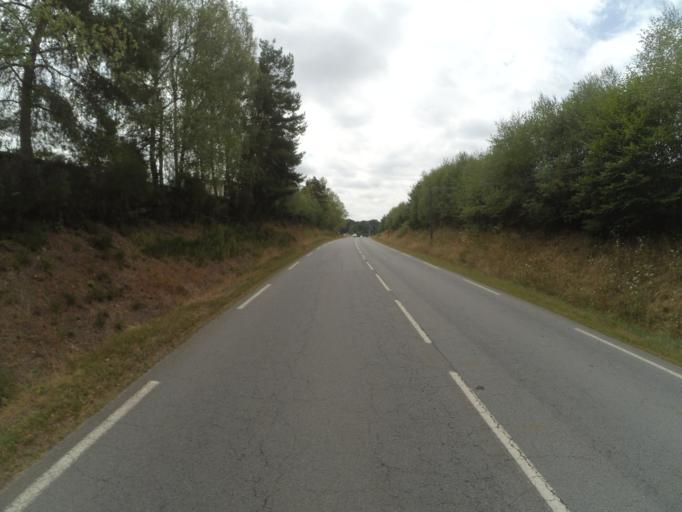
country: FR
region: Limousin
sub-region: Departement de la Correze
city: Ussel
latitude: 45.5769
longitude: 2.2946
